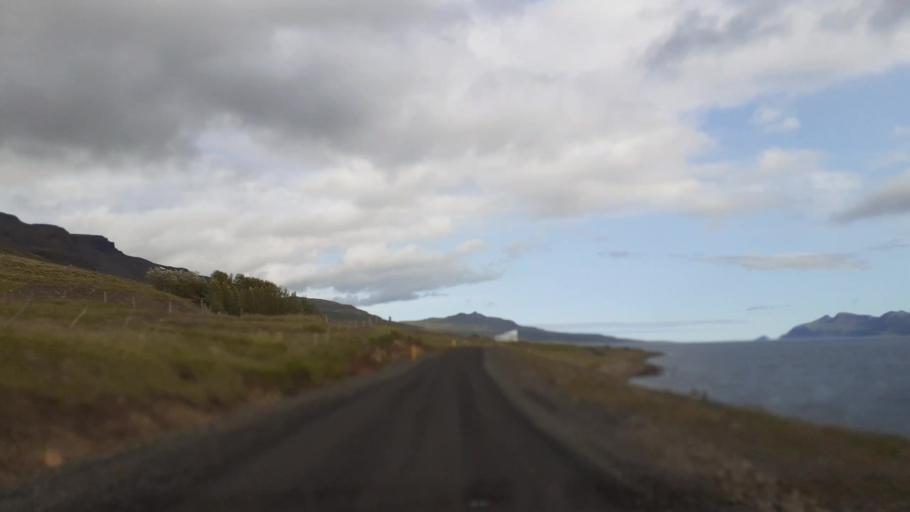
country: IS
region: East
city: Eskifjoerdur
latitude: 65.0548
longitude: -13.9718
